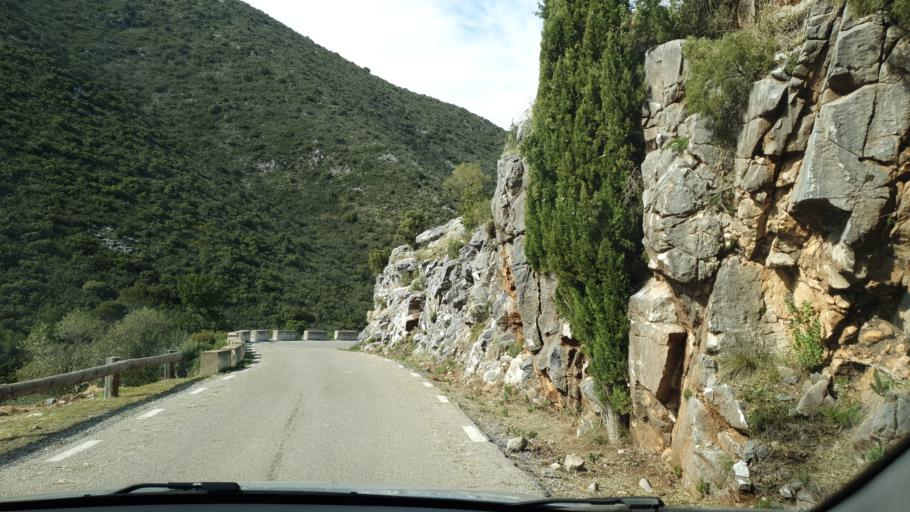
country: ES
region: Andalusia
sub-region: Provincia de Malaga
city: Ojen
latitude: 36.5857
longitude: -4.8816
